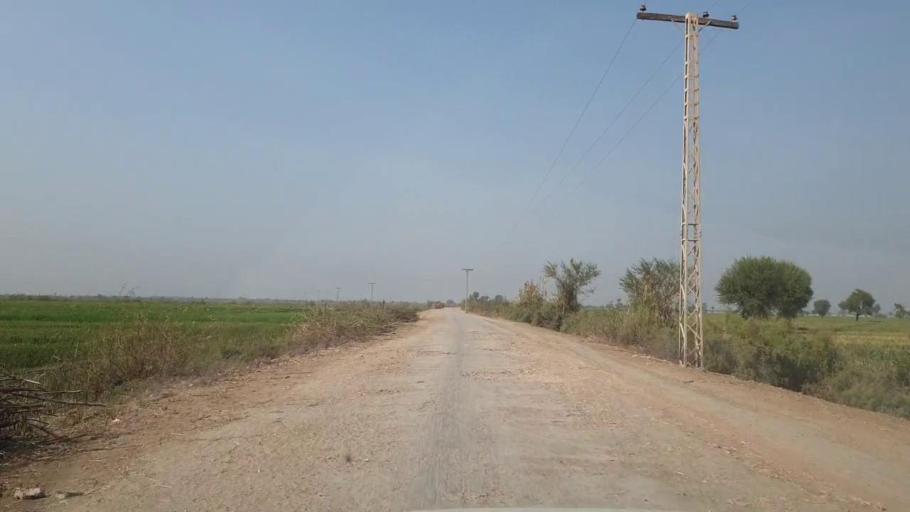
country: PK
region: Sindh
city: Mirpur Khas
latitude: 25.6931
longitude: 69.1491
